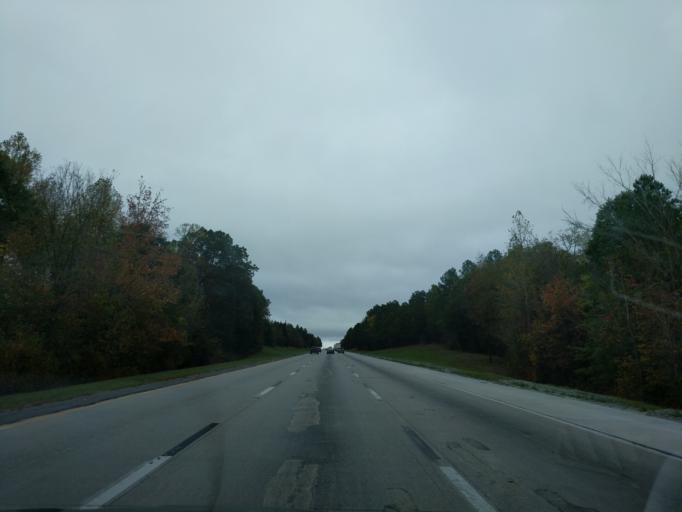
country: US
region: North Carolina
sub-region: Guilford County
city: Jamestown
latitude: 35.9466
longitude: -79.9008
